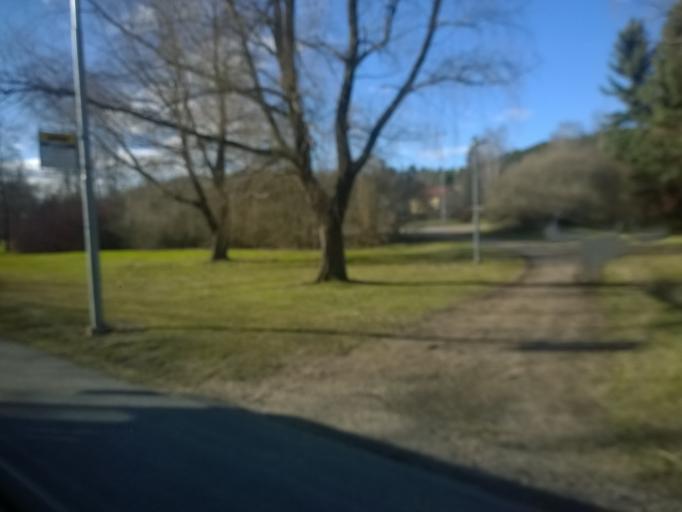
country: FI
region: Pirkanmaa
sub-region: Tampere
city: Tampere
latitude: 61.4879
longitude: 23.8052
